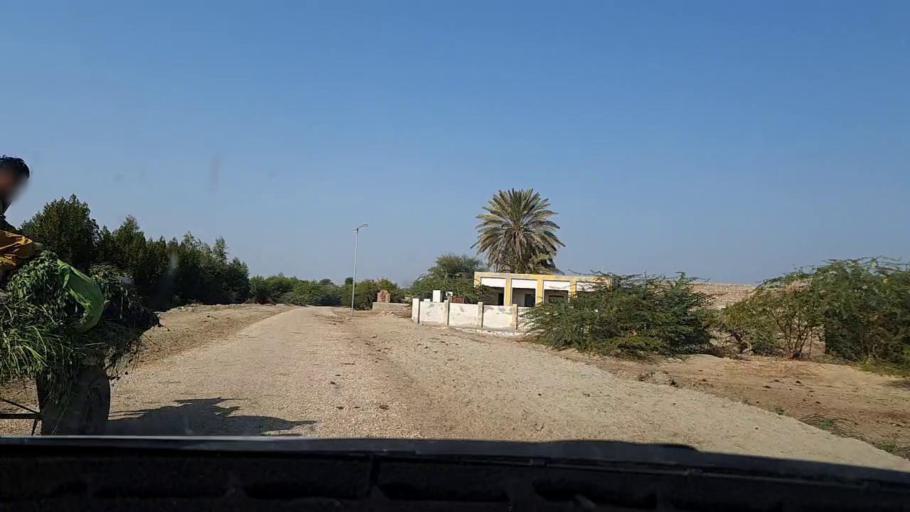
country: PK
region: Sindh
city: Tando Mittha Khan
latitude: 25.8301
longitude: 69.2880
